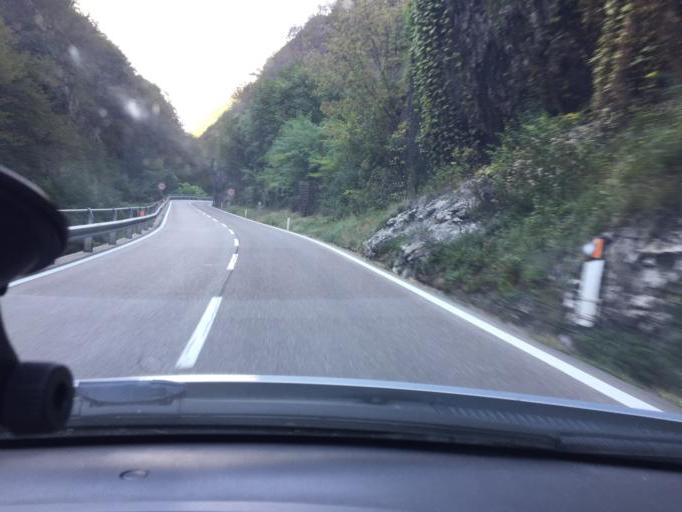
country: IT
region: Trentino-Alto Adige
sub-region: Provincia di Trento
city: Cadine
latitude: 46.0808
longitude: 11.0869
